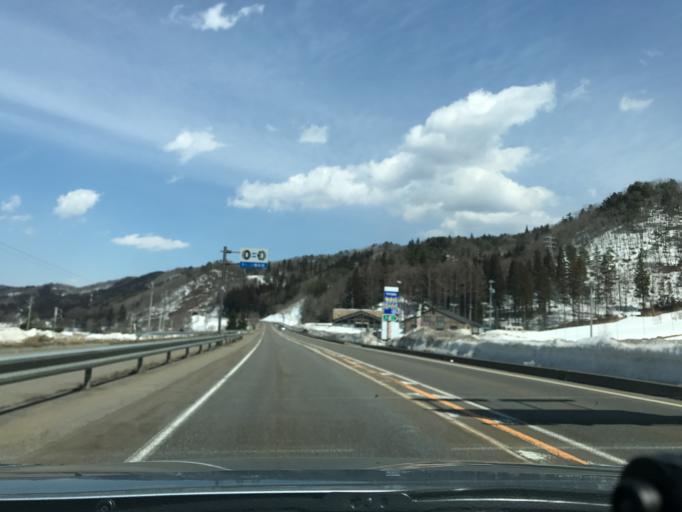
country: JP
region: Nagano
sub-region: Kitaazumi Gun
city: Hakuba
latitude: 36.6041
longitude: 137.8532
